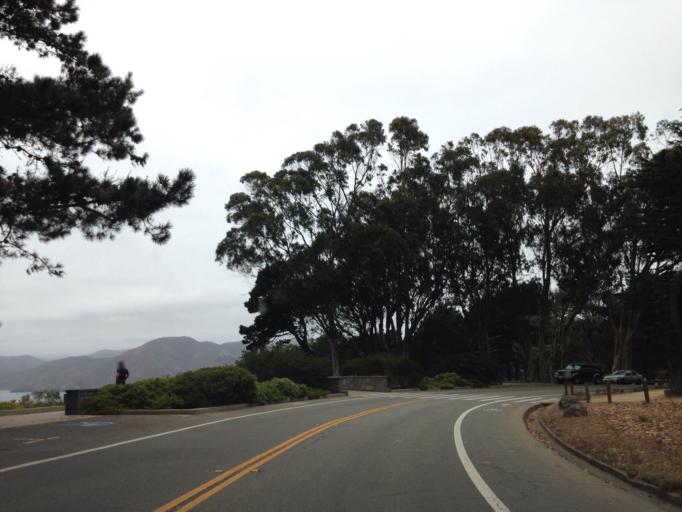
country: US
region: California
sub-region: San Francisco County
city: San Francisco
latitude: 37.7957
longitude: -122.4776
